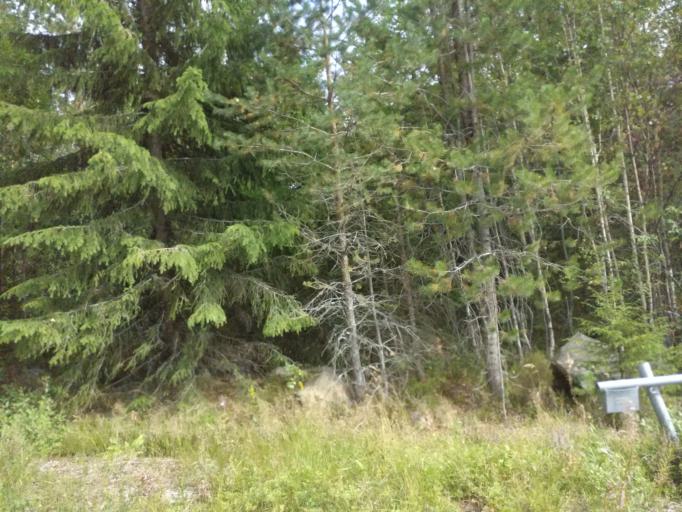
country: SE
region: Vaermland
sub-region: Hagfors Kommun
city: Hagfors
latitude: 60.0210
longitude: 13.7306
